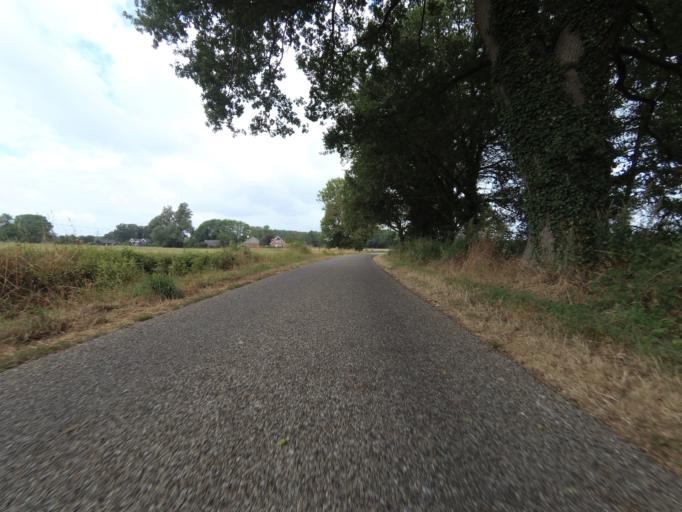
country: NL
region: Overijssel
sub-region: Gemeente Hengelo
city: Hengelo
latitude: 52.3092
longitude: 6.8402
